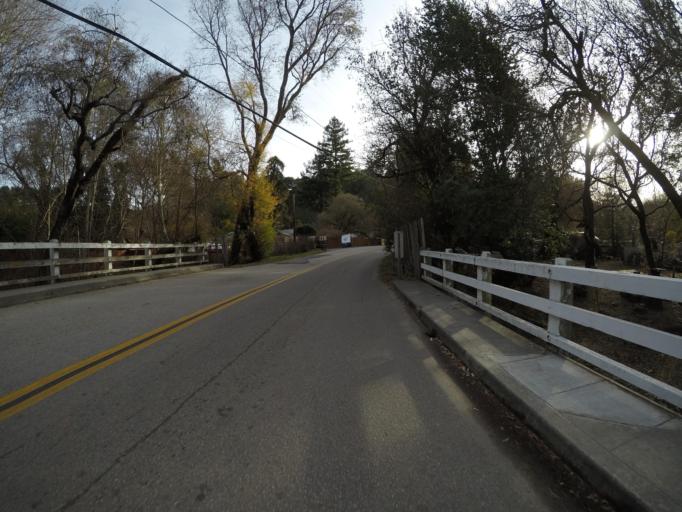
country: US
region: California
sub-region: Santa Cruz County
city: Scotts Valley
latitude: 37.0566
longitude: -122.0328
